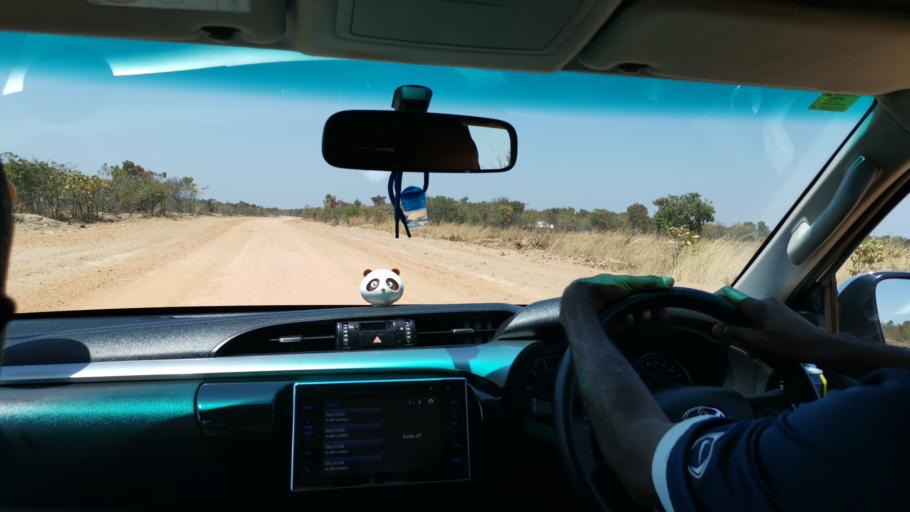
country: ZM
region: Central
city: Mkushi
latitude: -13.6414
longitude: 29.7537
